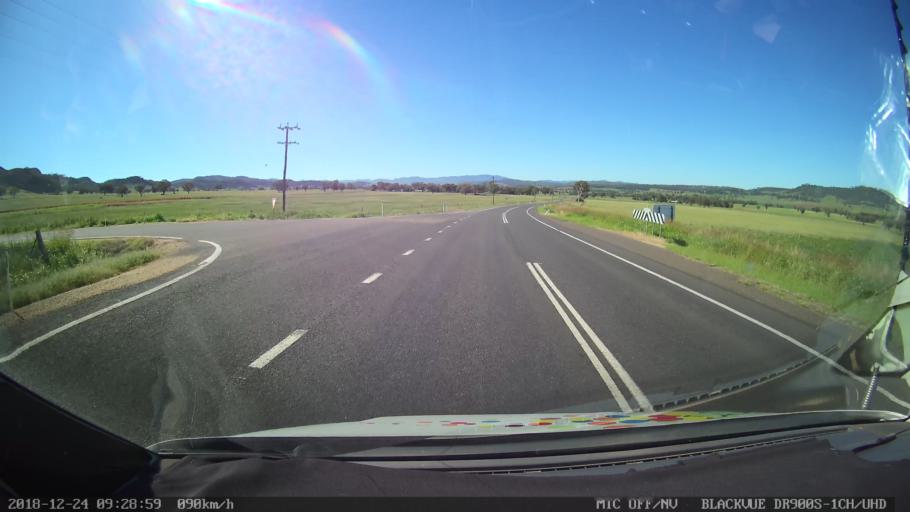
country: AU
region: New South Wales
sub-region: Liverpool Plains
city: Quirindi
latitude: -31.5442
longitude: 150.6926
